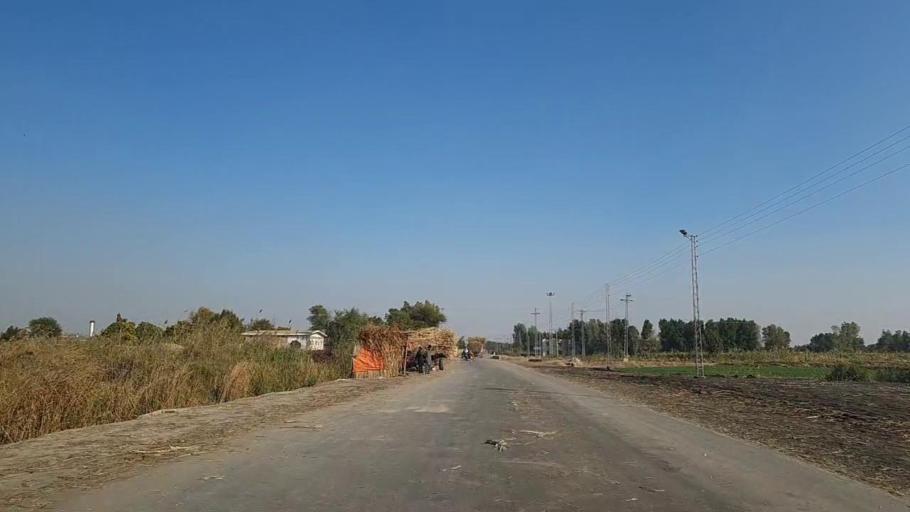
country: PK
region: Sindh
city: Bandhi
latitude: 26.6052
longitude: 68.3114
